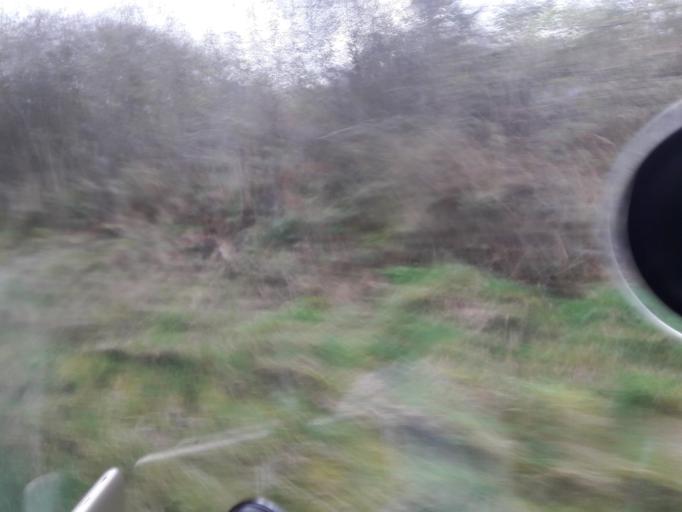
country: IE
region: Leinster
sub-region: An Iarmhi
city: An Muileann gCearr
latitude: 53.6095
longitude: -7.4048
